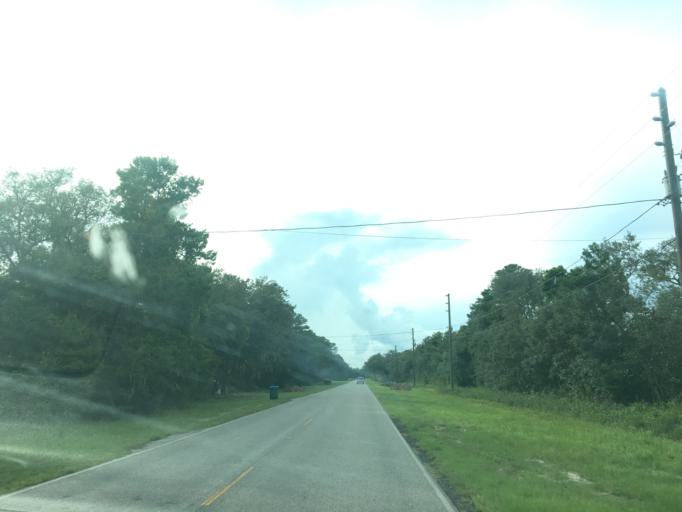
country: US
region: Florida
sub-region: Wakulla County
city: Crawfordville
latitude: 29.9080
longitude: -84.3584
